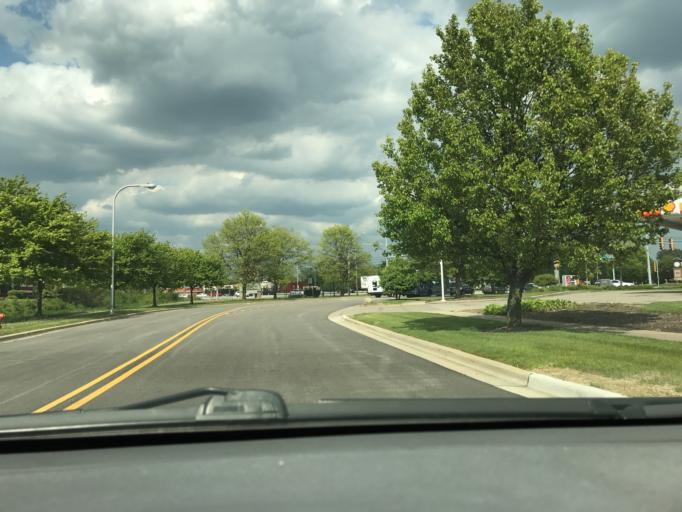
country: US
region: Illinois
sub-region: Kane County
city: South Elgin
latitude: 42.0249
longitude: -88.3403
